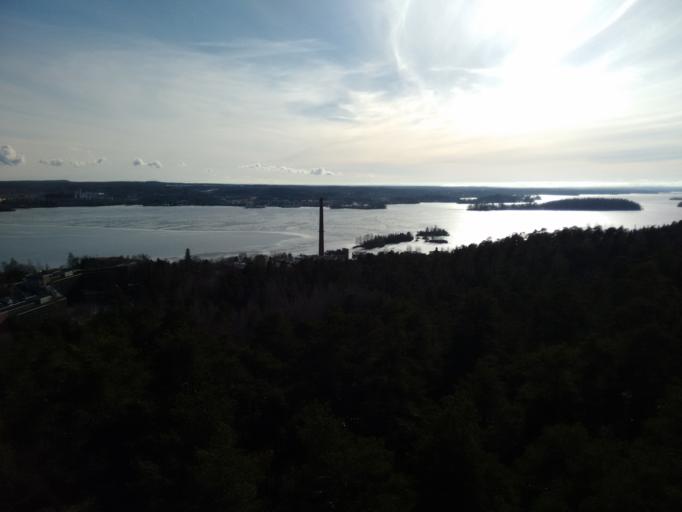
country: FI
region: Pirkanmaa
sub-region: Tampere
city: Tampere
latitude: 61.4943
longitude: 23.7346
